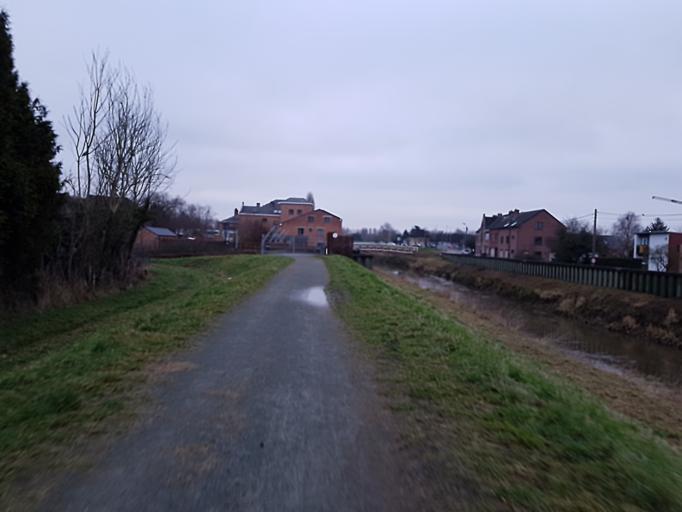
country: BE
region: Flanders
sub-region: Provincie Vlaams-Brabant
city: Tremelo
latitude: 50.9713
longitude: 4.6904
